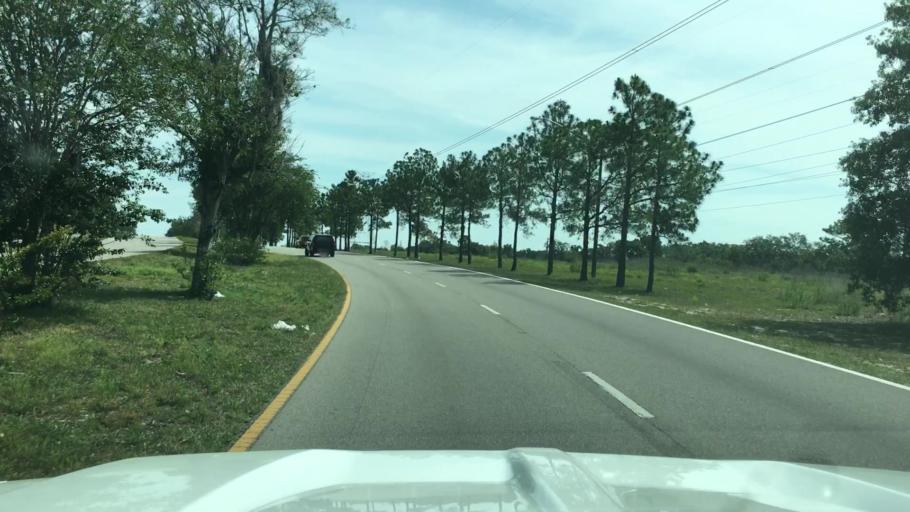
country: US
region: Florida
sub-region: Pasco County
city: Shady Hills
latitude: 28.4382
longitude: -82.5448
